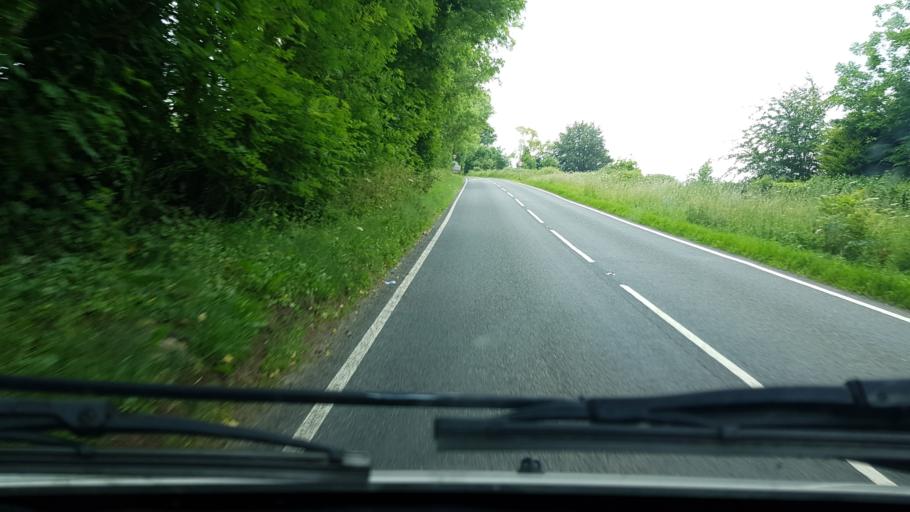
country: GB
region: England
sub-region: Gloucestershire
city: Stow on the Wold
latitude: 51.9381
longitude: -1.7281
